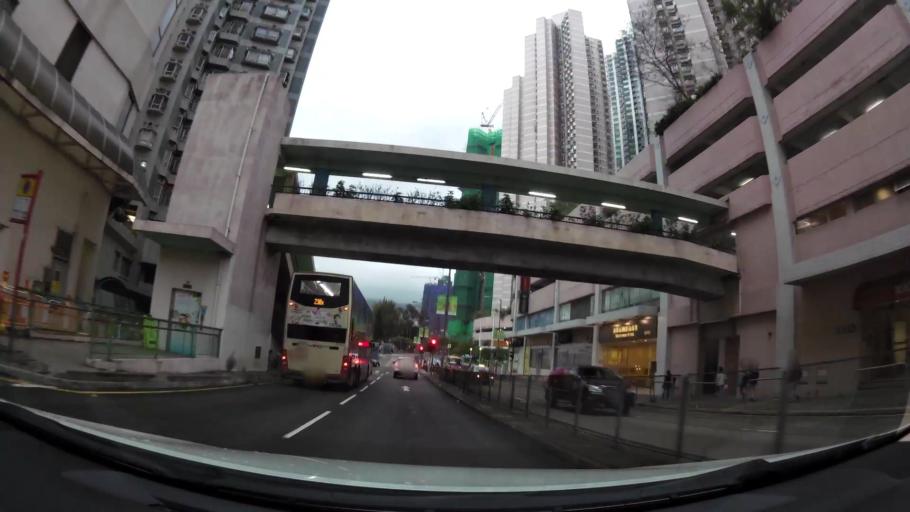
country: HK
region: Tsuen Wan
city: Tsuen Wan
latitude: 22.3635
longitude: 114.1146
